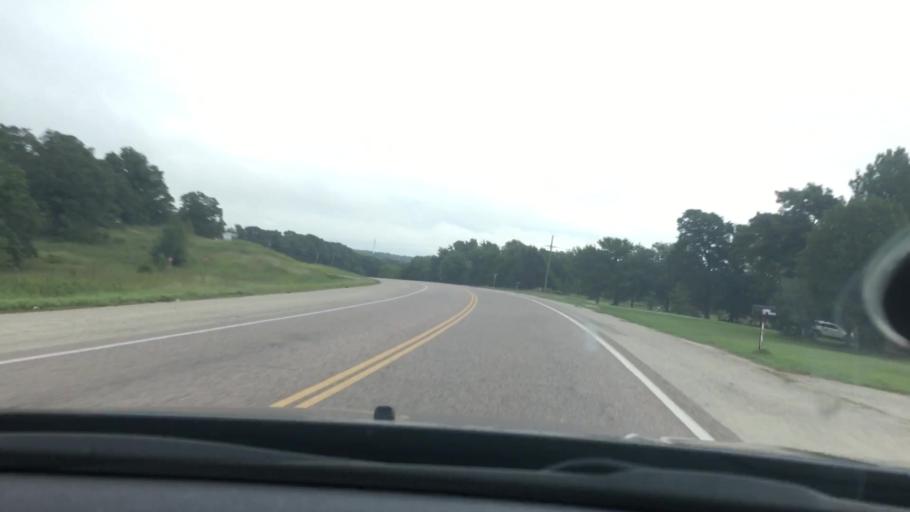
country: US
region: Oklahoma
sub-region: Pontotoc County
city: Ada
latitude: 34.7832
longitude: -96.5754
